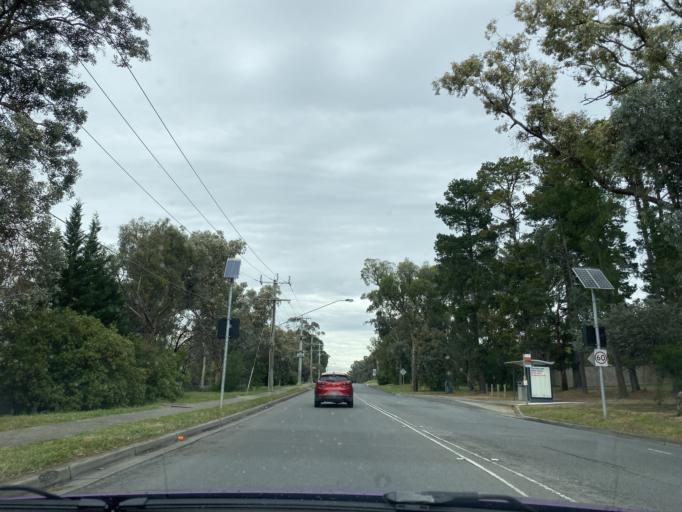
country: AU
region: Victoria
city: Saint Helena
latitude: -37.6863
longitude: 145.1365
